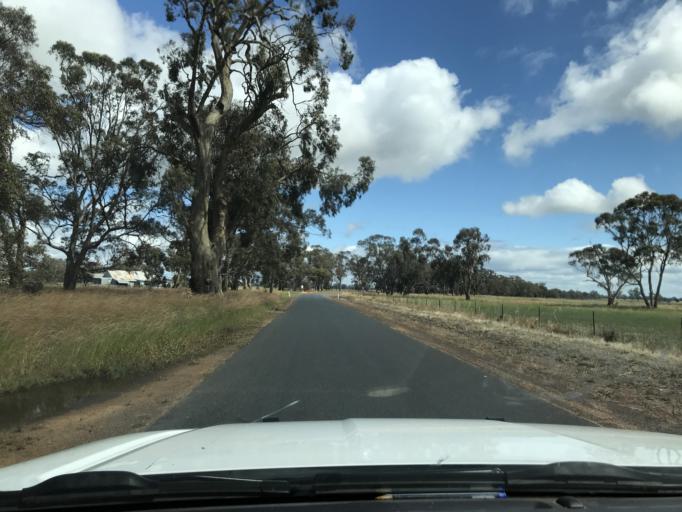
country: AU
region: Victoria
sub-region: Horsham
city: Horsham
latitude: -36.8070
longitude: 141.4795
